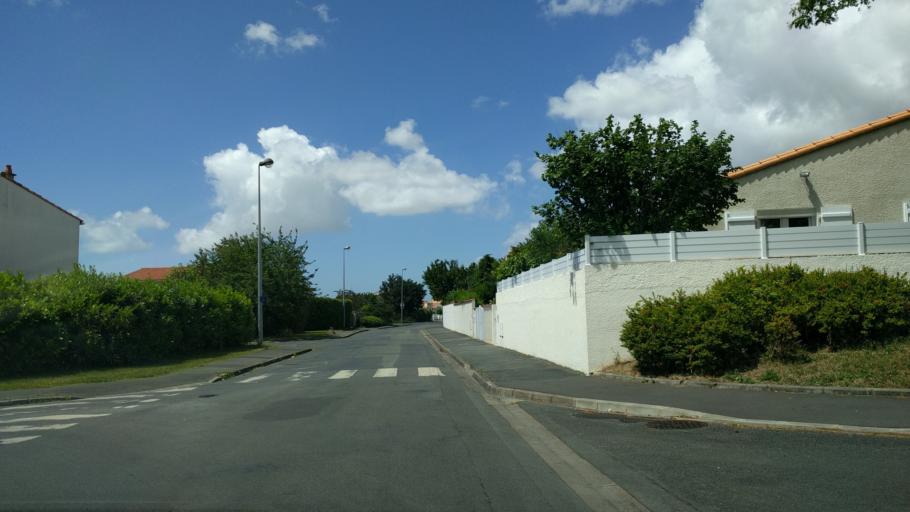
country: FR
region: Poitou-Charentes
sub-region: Departement de la Charente-Maritime
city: Puilboreau
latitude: 46.1680
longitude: -1.1244
